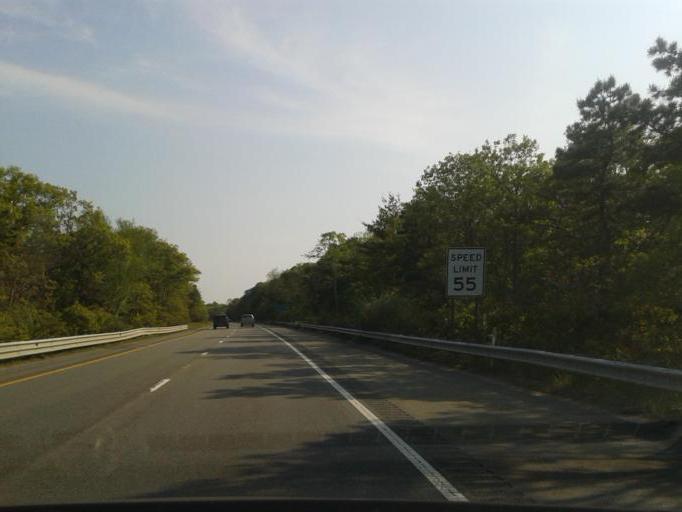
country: US
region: Massachusetts
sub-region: Barnstable County
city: West Falmouth
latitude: 41.6093
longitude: -70.6248
